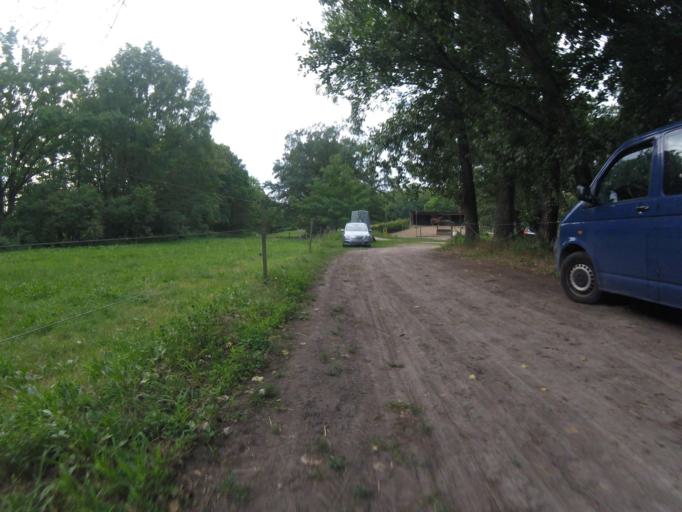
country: DE
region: Brandenburg
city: Mittenwalde
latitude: 52.2923
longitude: 13.5498
